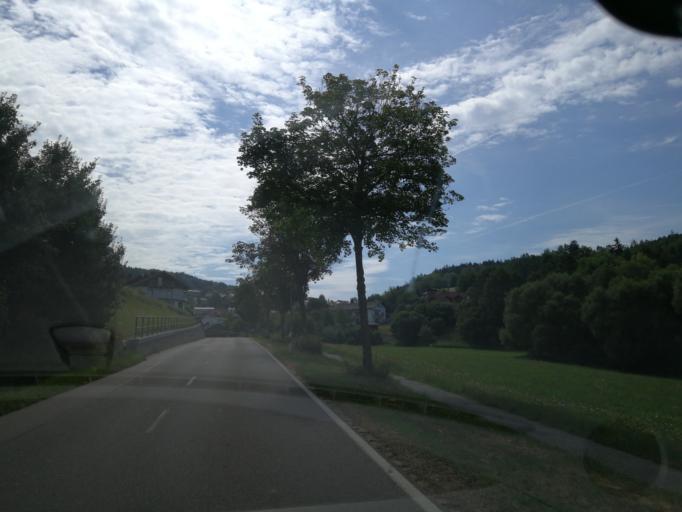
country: DE
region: Bavaria
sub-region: Upper Palatinate
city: Falkenstein
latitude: 49.0986
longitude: 12.4811
